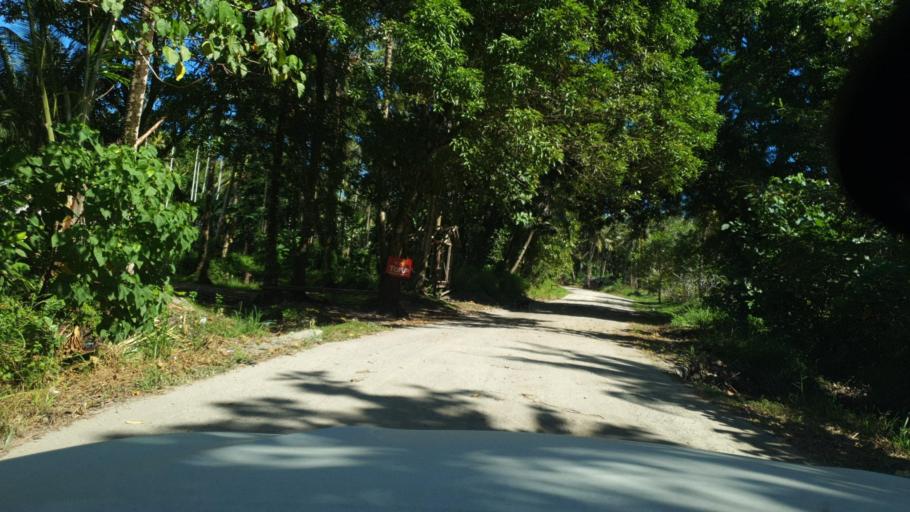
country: SB
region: Guadalcanal
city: Honiara
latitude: -9.2724
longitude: 159.6519
